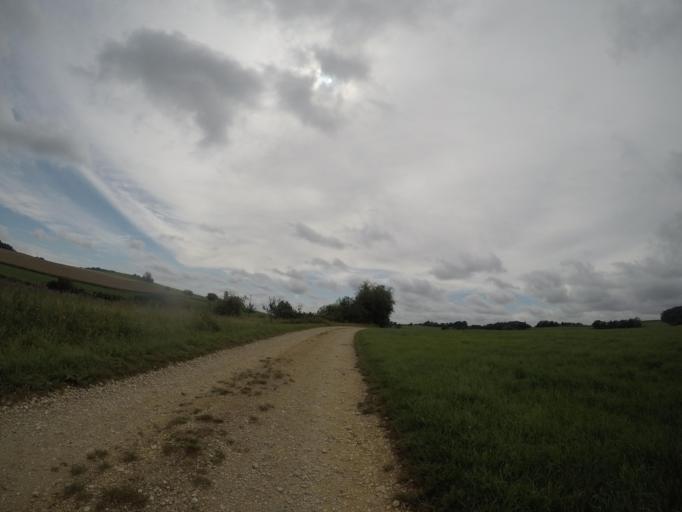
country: DE
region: Baden-Wuerttemberg
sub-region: Tuebingen Region
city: Laichingen
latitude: 48.4623
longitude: 9.6487
